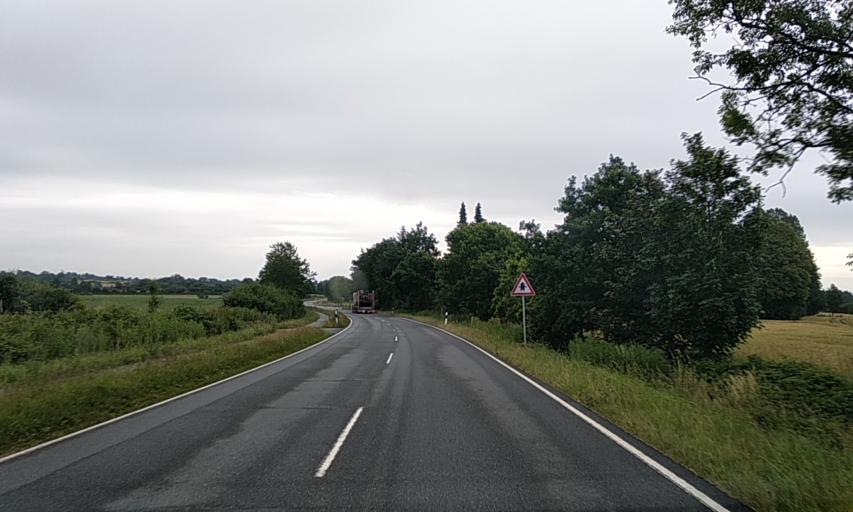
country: DE
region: Schleswig-Holstein
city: Struxdorf
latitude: 54.6314
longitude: 9.6532
